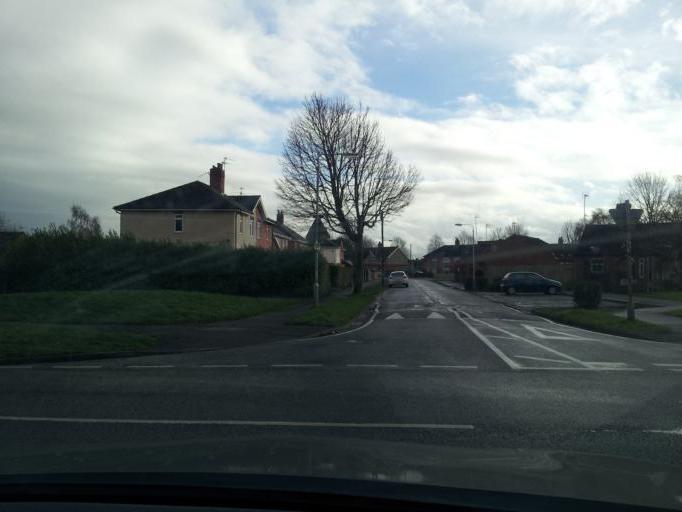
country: GB
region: England
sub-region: Nottinghamshire
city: Newark on Trent
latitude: 53.0651
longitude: -0.8091
